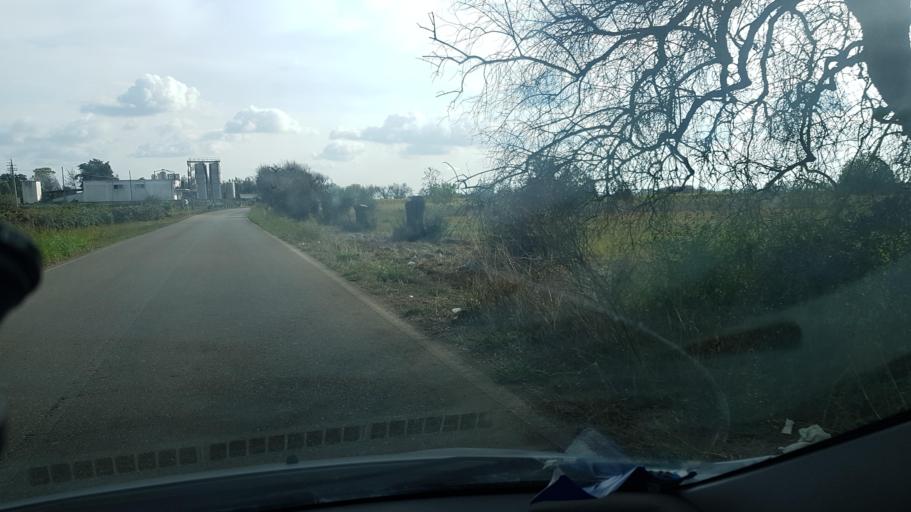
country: IT
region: Apulia
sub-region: Provincia di Brindisi
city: Cellino San Marco
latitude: 40.4615
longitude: 17.9574
